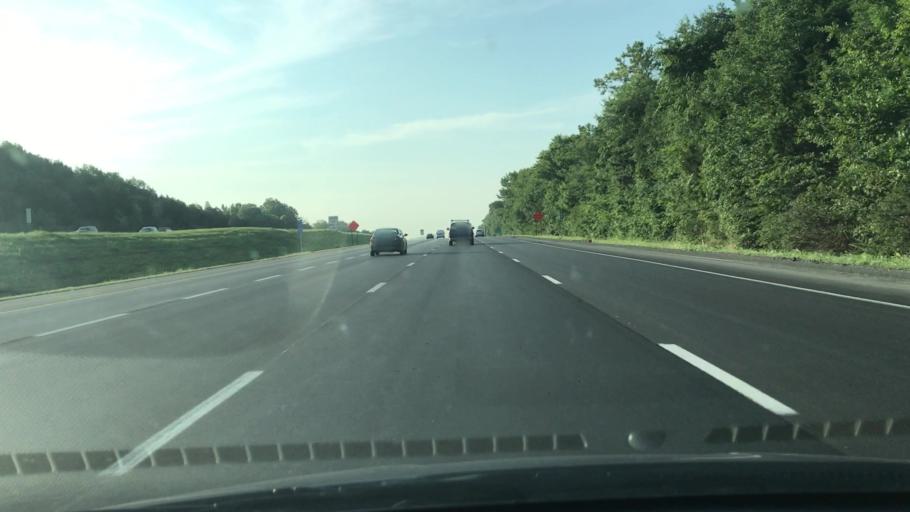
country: US
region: Tennessee
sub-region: Rutherford County
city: Smyrna
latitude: 35.9451
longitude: -86.5440
